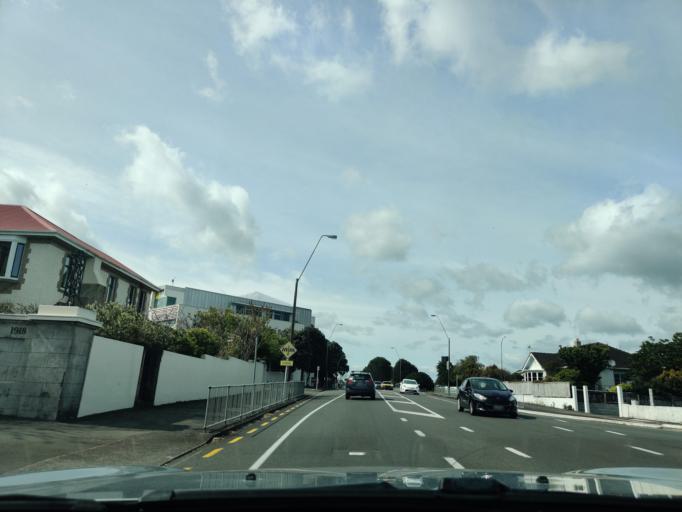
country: NZ
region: Taranaki
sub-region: New Plymouth District
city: New Plymouth
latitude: -39.0606
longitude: 174.0855
